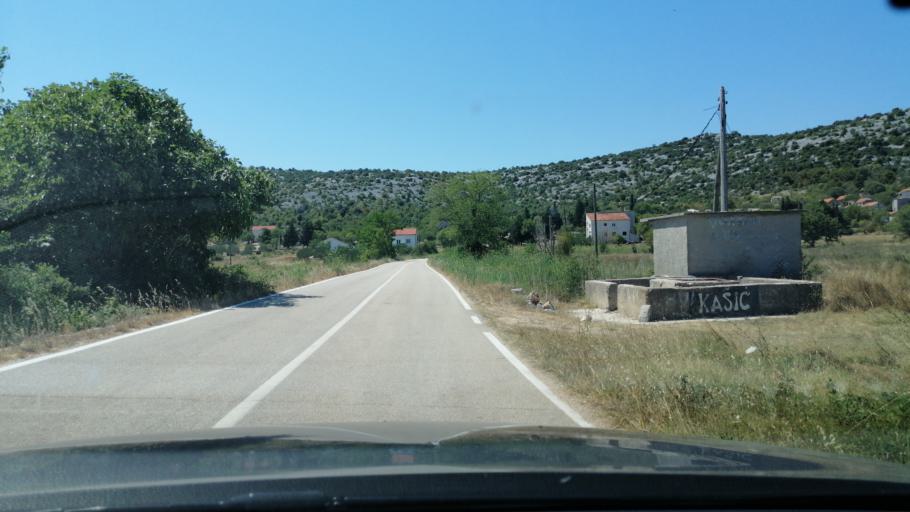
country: HR
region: Sibensko-Kniniska
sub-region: Grad Sibenik
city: Pirovac
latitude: 43.8728
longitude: 15.6812
